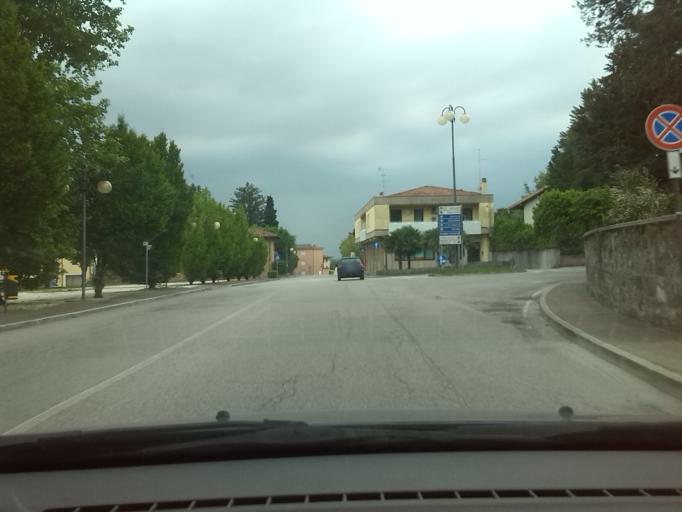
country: IT
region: Friuli Venezia Giulia
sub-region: Provincia di Udine
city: Santo Stefano
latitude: 46.2067
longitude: 13.1247
